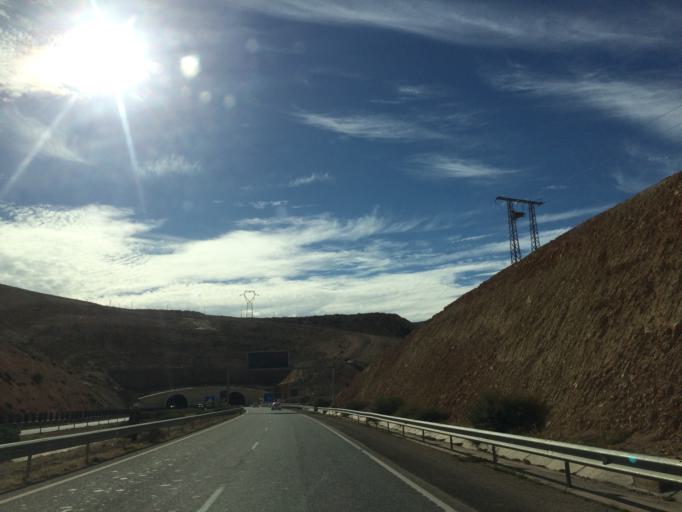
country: MA
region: Marrakech-Tensift-Al Haouz
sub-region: Chichaoua
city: Taouloukoult
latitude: 31.1940
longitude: -8.9789
